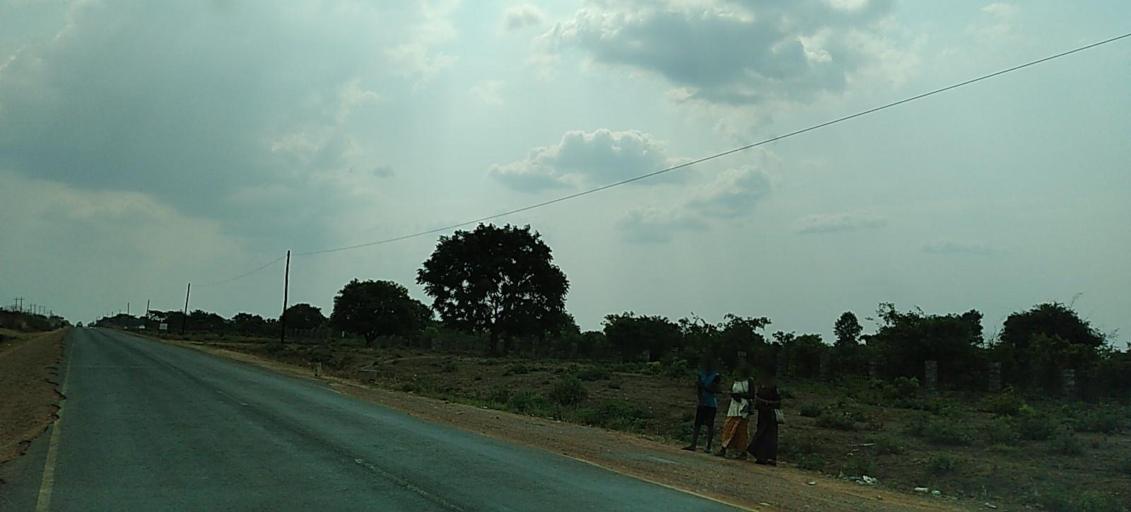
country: ZM
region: Copperbelt
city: Kalulushi
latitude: -12.8494
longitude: 28.1288
